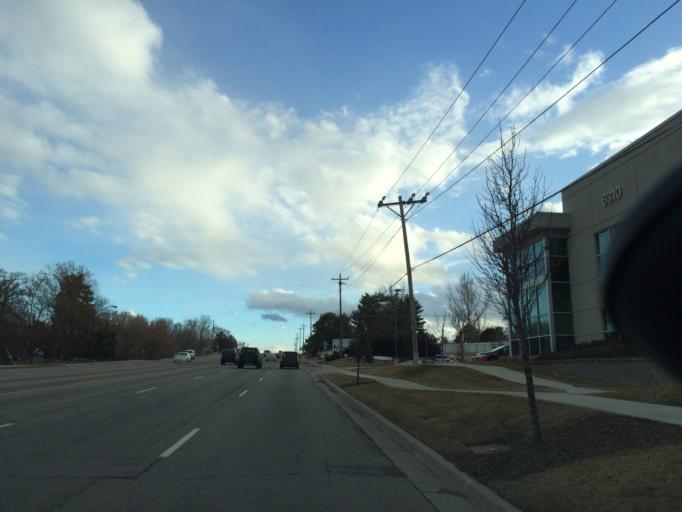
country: US
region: Utah
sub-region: Salt Lake County
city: West Jordan
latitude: 40.6358
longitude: -111.9390
